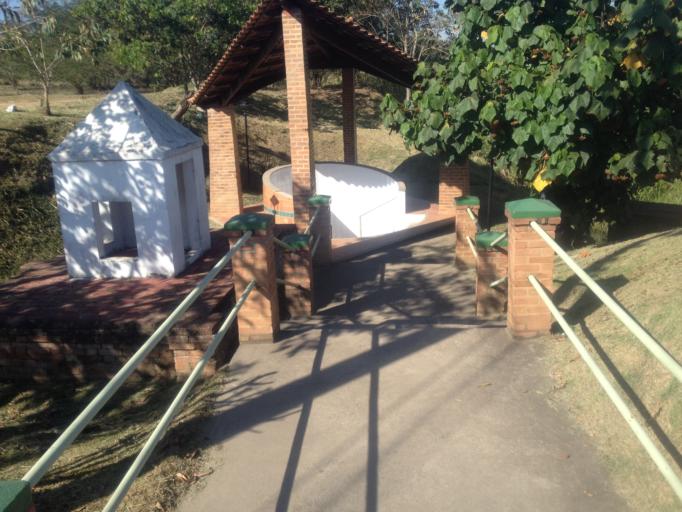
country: BR
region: Rio de Janeiro
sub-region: Porto Real
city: Porto Real
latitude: -22.4160
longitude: -44.3245
